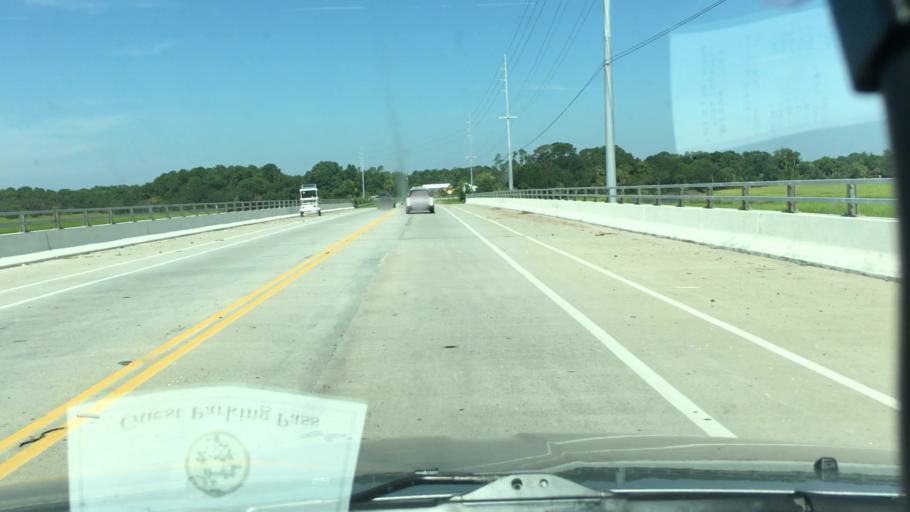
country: US
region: South Carolina
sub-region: Beaufort County
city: Beaufort
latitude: 32.3979
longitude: -80.6154
